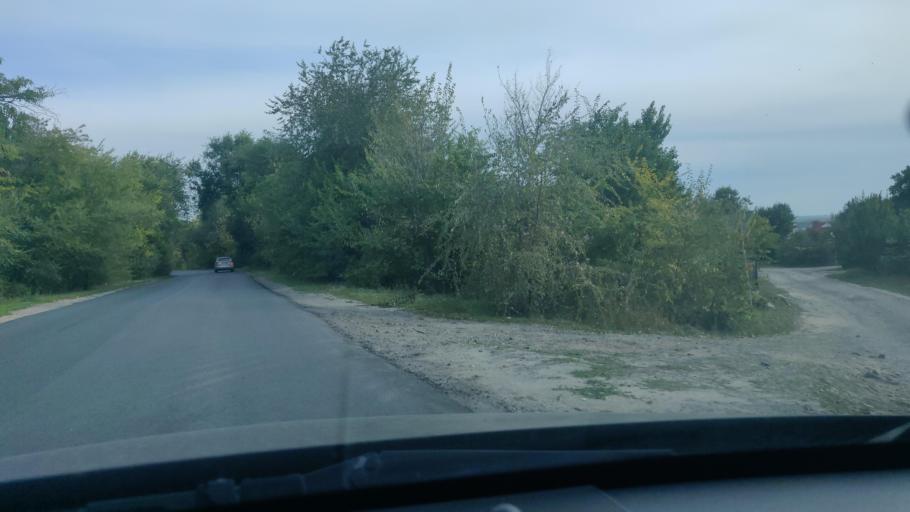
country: RU
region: Rostov
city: Ust'-Donetskiy
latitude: 47.6471
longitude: 40.8804
